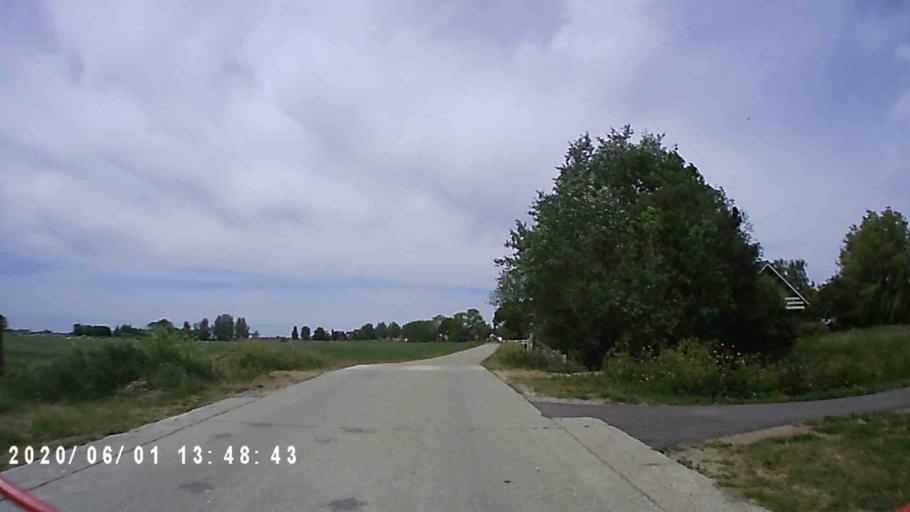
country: NL
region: Friesland
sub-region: Gemeente Littenseradiel
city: Wommels
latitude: 53.0935
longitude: 5.6196
